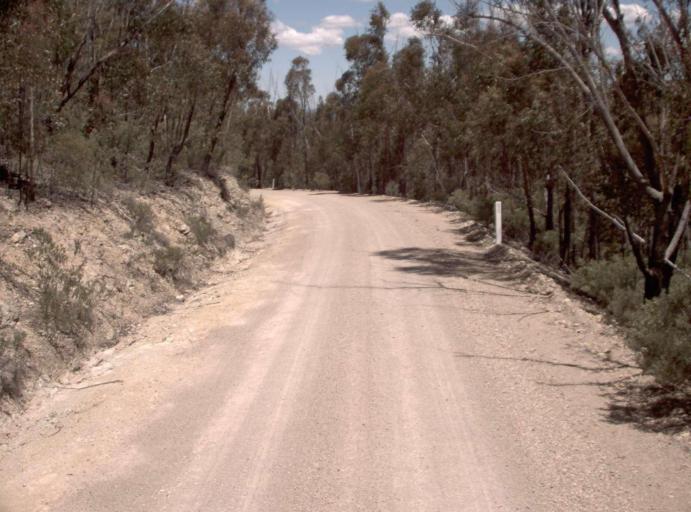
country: AU
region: New South Wales
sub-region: Snowy River
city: Jindabyne
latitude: -37.0871
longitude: 148.3271
